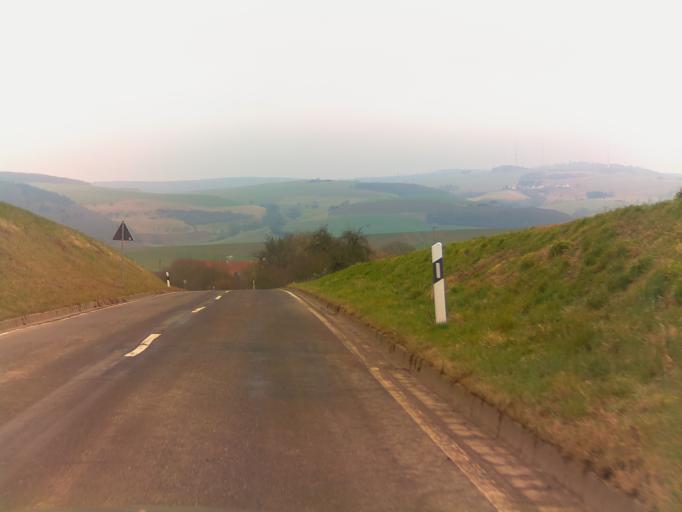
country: DE
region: Rheinland-Pfalz
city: Sankt Alban
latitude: 49.6898
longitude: 7.8437
